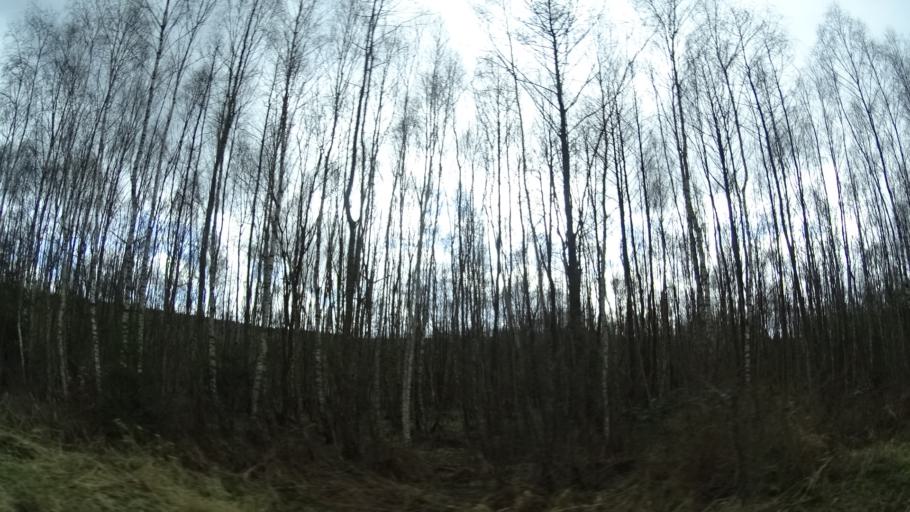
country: DE
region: Rheinland-Pfalz
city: Schnorbach
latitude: 49.9544
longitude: 7.6593
